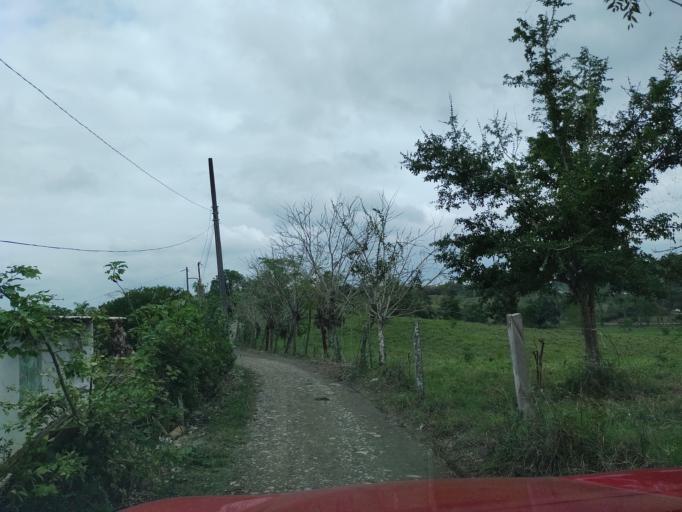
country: MX
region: Veracruz
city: Coatzintla
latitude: 20.4579
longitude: -97.4151
